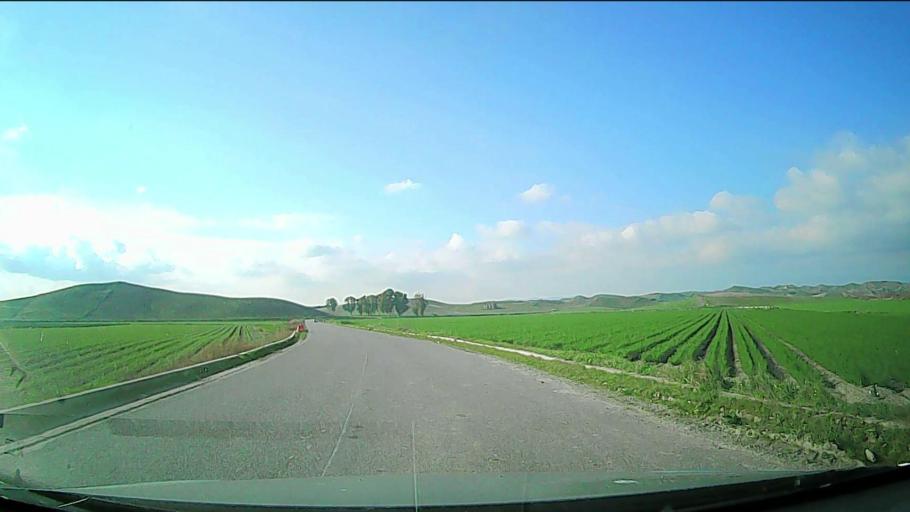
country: IT
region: Calabria
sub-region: Provincia di Crotone
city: Tronca
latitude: 39.1999
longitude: 17.0662
